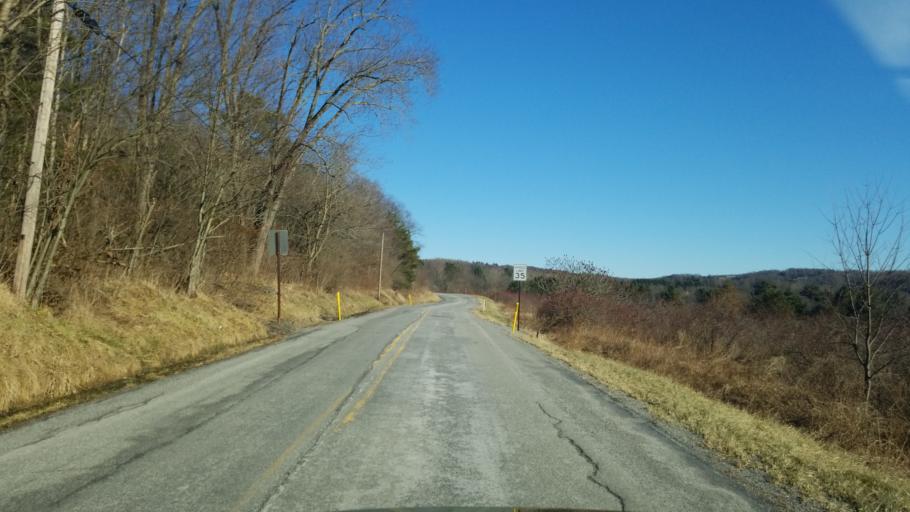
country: US
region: Pennsylvania
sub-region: Jefferson County
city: Sykesville
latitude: 41.0476
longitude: -78.7692
